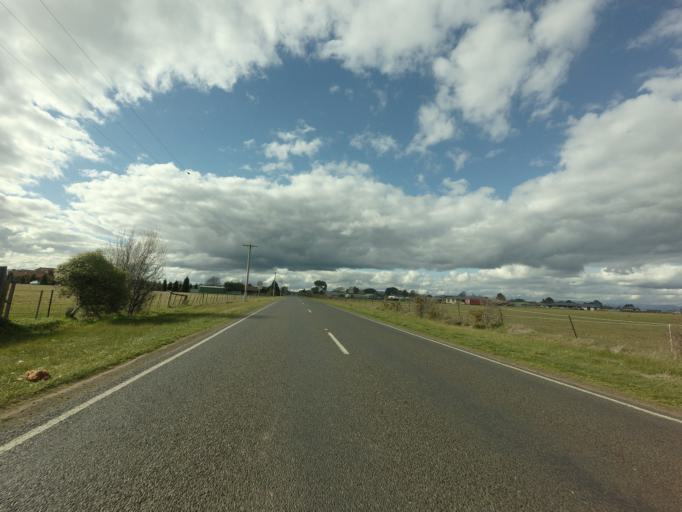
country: AU
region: Tasmania
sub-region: Northern Midlands
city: Longford
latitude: -41.6119
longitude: 147.1142
